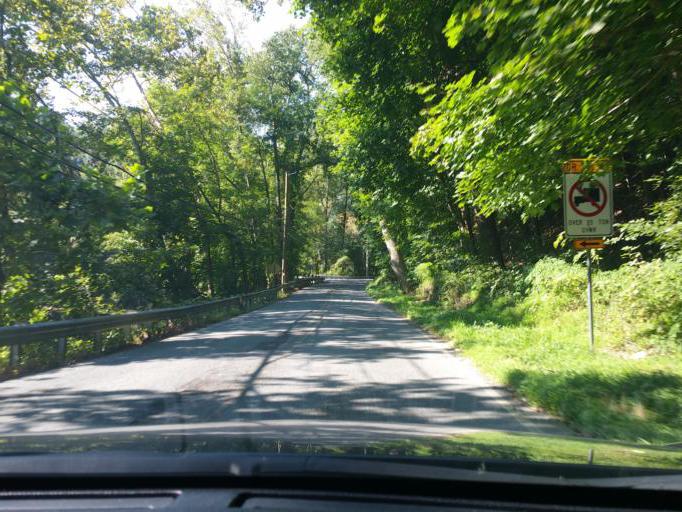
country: US
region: Maryland
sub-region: Cecil County
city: Rising Sun
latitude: 39.6628
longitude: -76.1476
